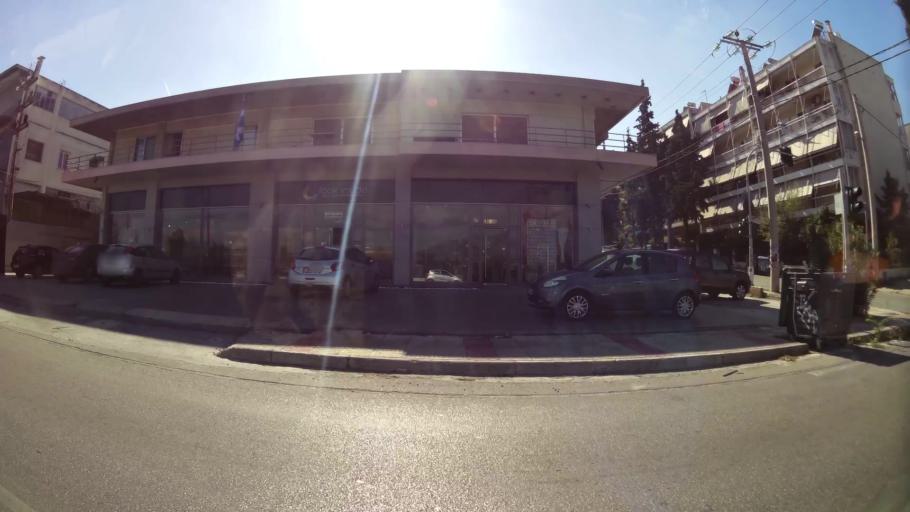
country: GR
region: Attica
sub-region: Nomarchia Athinas
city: Lykovrysi
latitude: 38.0687
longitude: 23.7745
